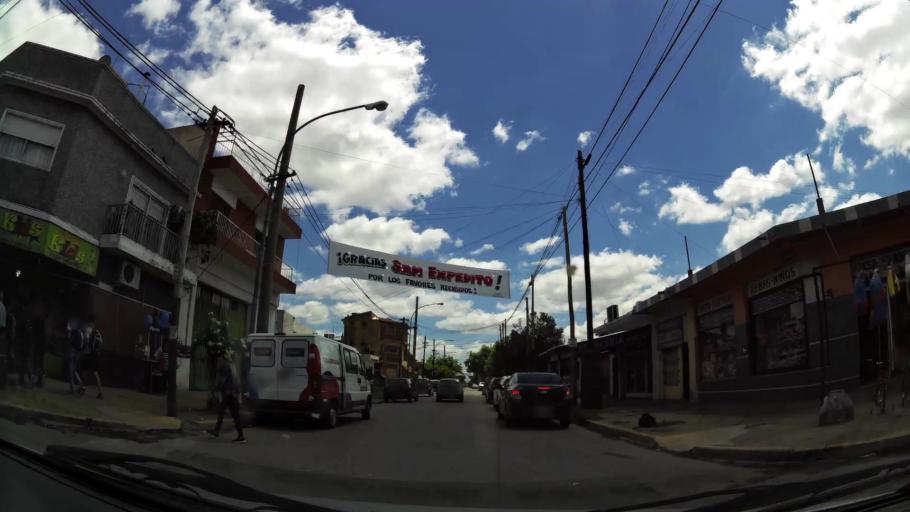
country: AR
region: Buenos Aires
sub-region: Partido de Lanus
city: Lanus
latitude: -34.7116
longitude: -58.4245
